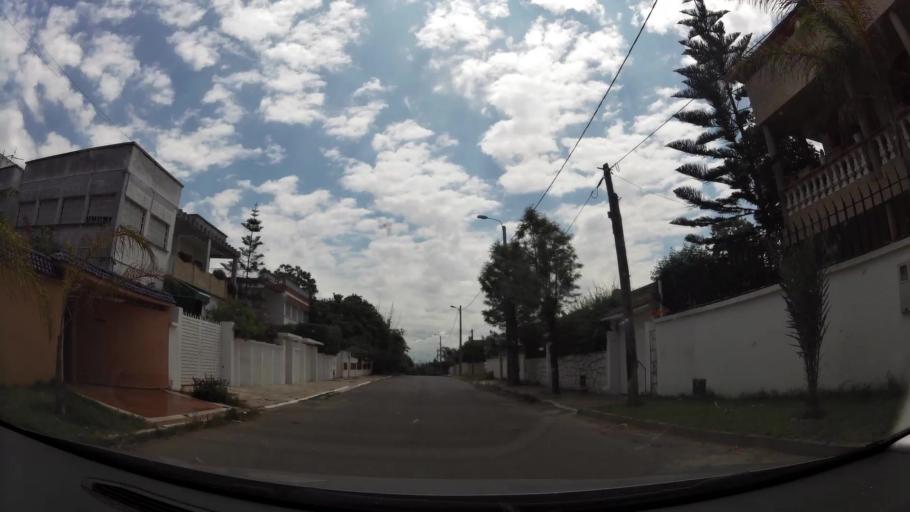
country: MA
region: Gharb-Chrarda-Beni Hssen
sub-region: Kenitra Province
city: Kenitra
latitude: 34.2647
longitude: -6.5973
